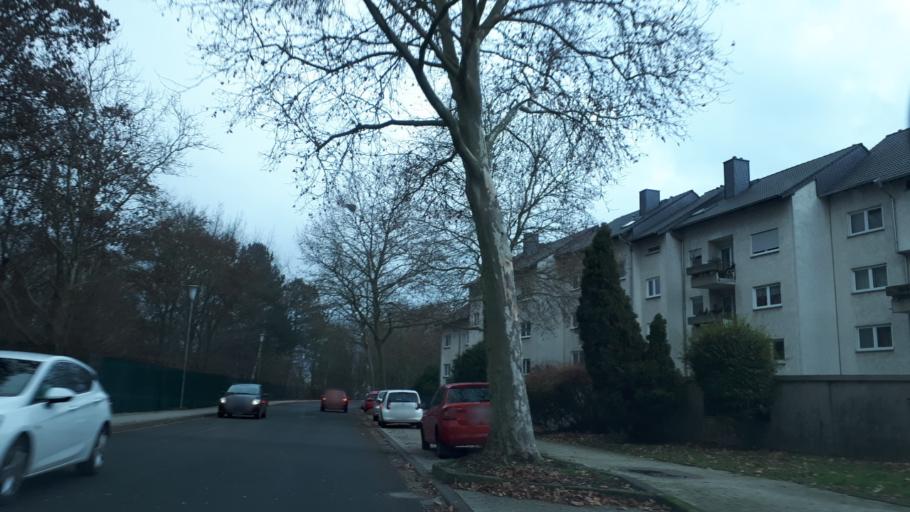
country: DE
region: Rheinland-Pfalz
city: Andernach
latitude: 50.4282
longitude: 7.3949
